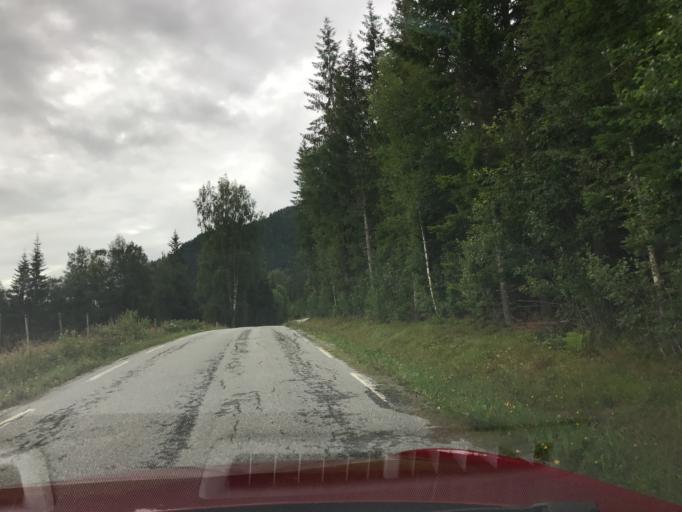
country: NO
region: Buskerud
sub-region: Rollag
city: Rollag
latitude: 60.0690
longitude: 9.1098
